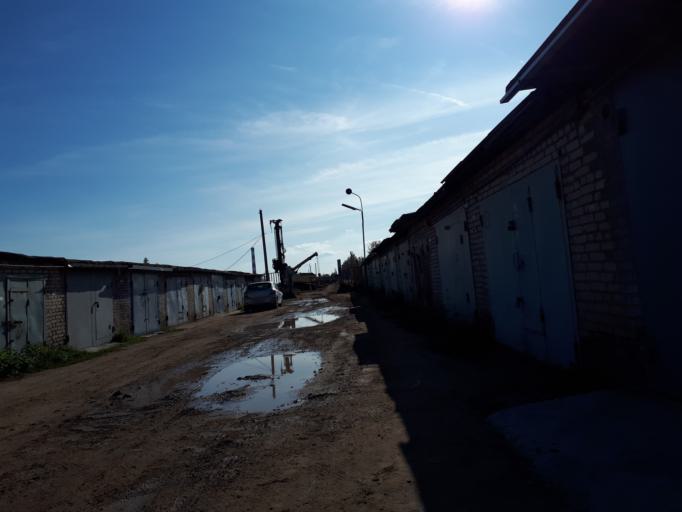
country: BY
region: Vitebsk
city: Vitebsk
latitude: 55.1684
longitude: 30.2456
